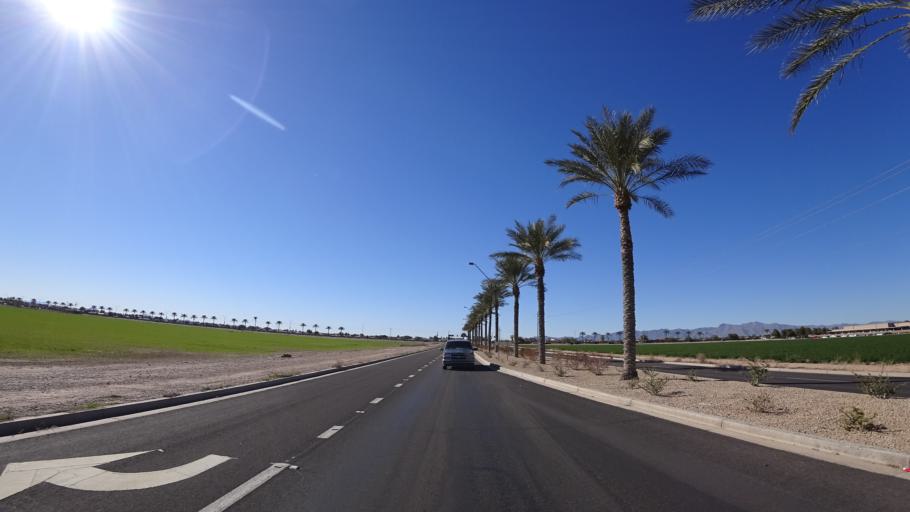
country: US
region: Arizona
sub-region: Maricopa County
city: Goodyear
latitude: 33.4355
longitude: -112.3891
